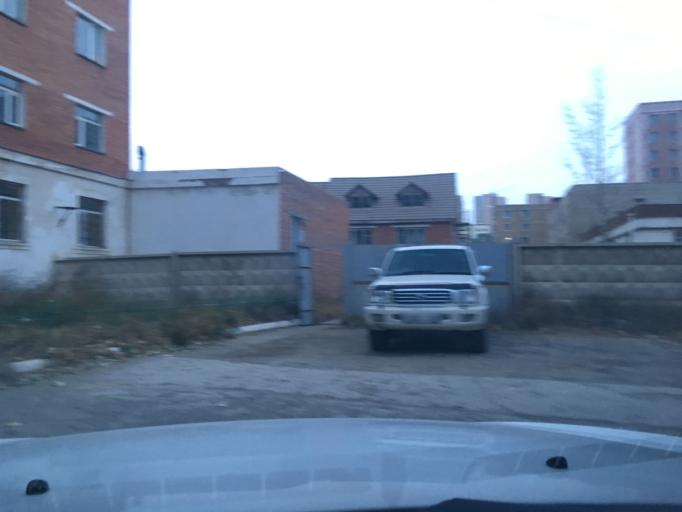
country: MN
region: Ulaanbaatar
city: Ulaanbaatar
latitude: 47.9161
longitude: 106.8589
